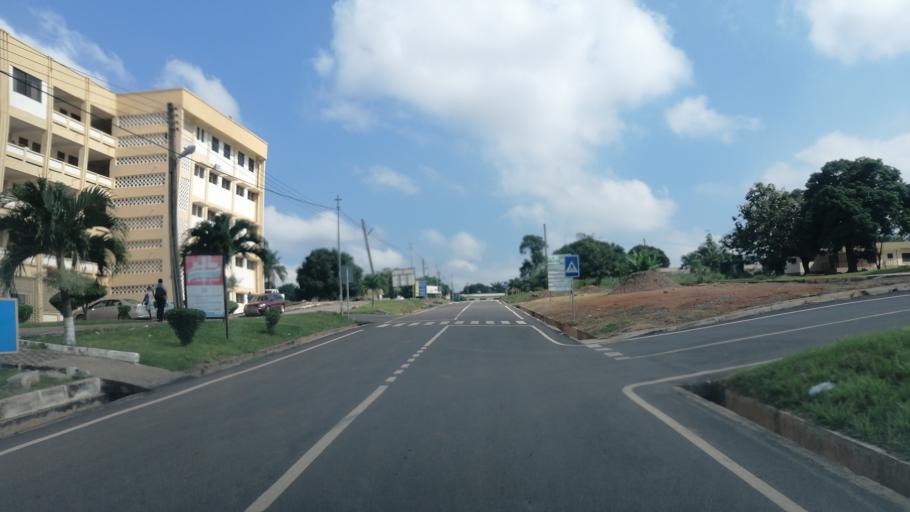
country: GH
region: Ashanti
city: Kumasi
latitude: 6.7000
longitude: -1.6819
